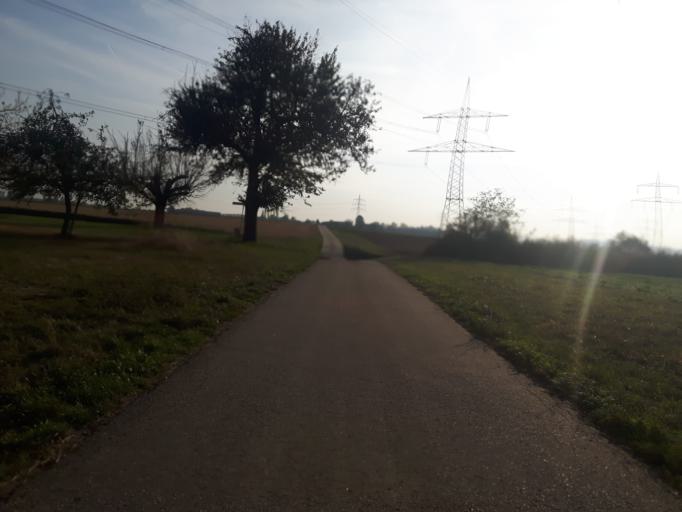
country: DE
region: Baden-Wuerttemberg
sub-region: Regierungsbezirk Stuttgart
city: Untereisesheim
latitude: 49.1750
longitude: 9.1748
